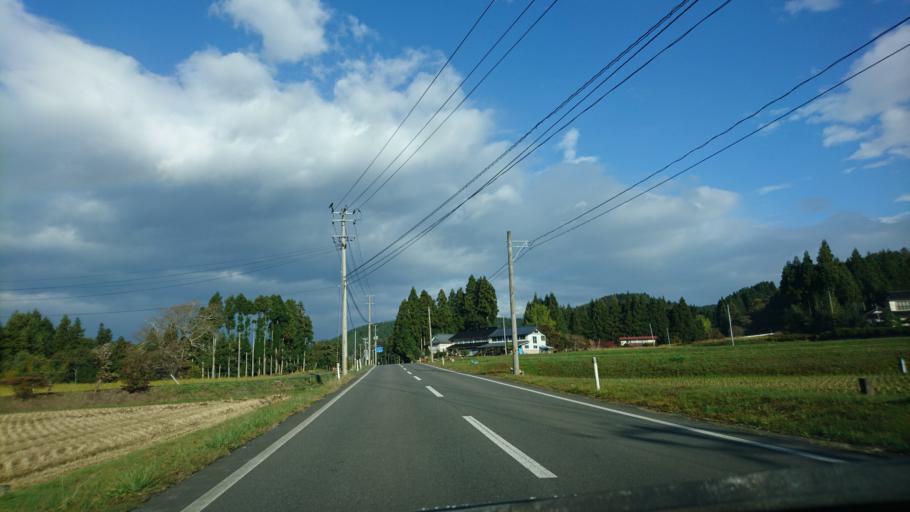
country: JP
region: Iwate
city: Mizusawa
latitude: 39.0519
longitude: 141.0457
